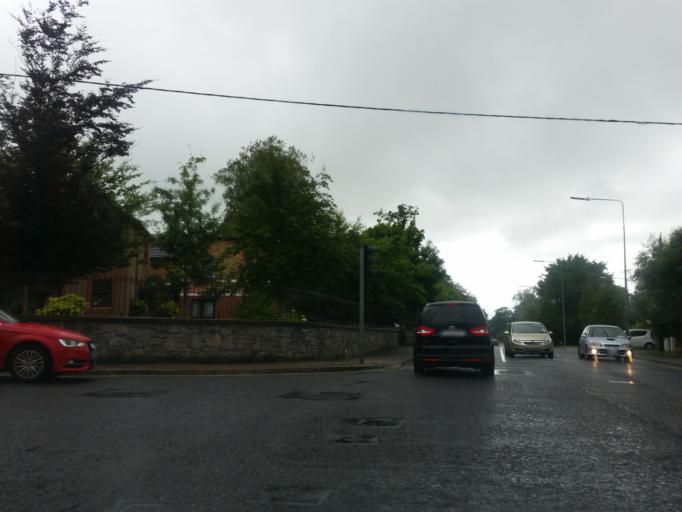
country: IE
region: Connaught
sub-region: Sligo
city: Sligo
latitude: 54.2710
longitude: -8.4967
